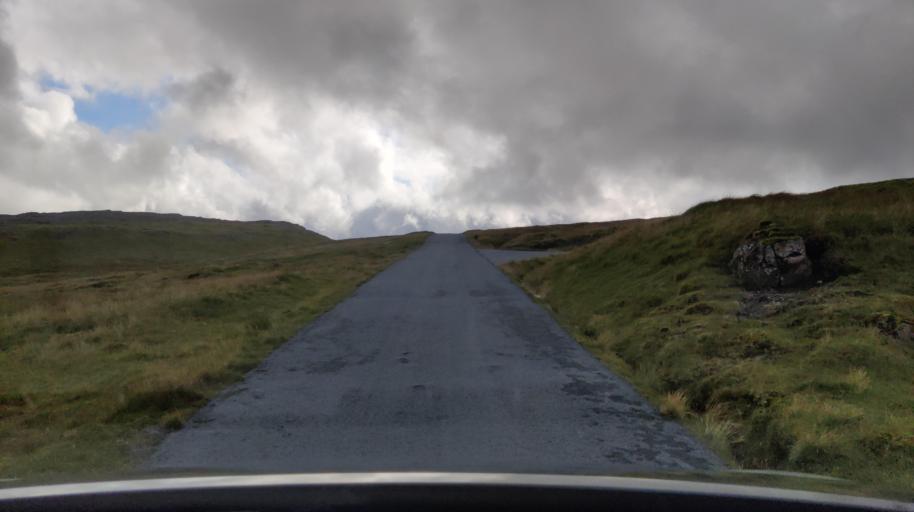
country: FO
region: Streymoy
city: Vestmanna
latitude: 62.1714
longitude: -7.1593
